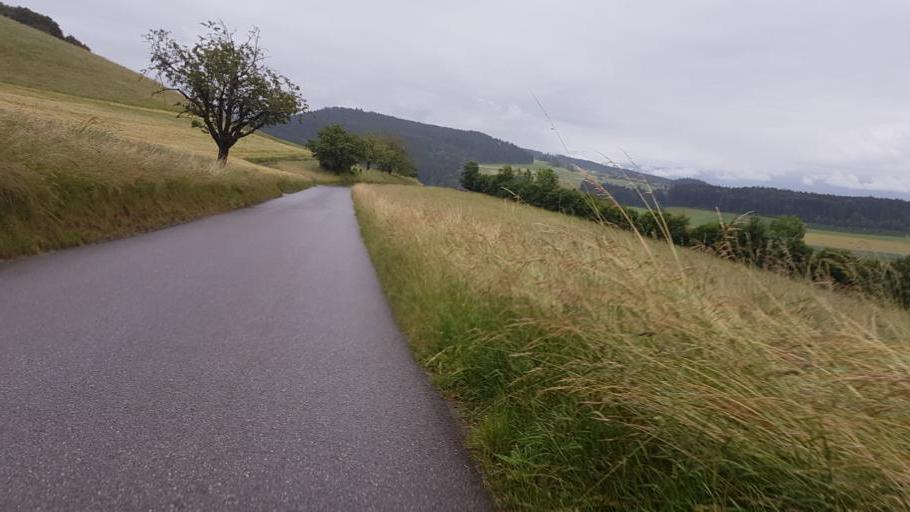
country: CH
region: Bern
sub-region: Bern-Mittelland District
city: Taegertschi
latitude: 46.8812
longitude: 7.5936
